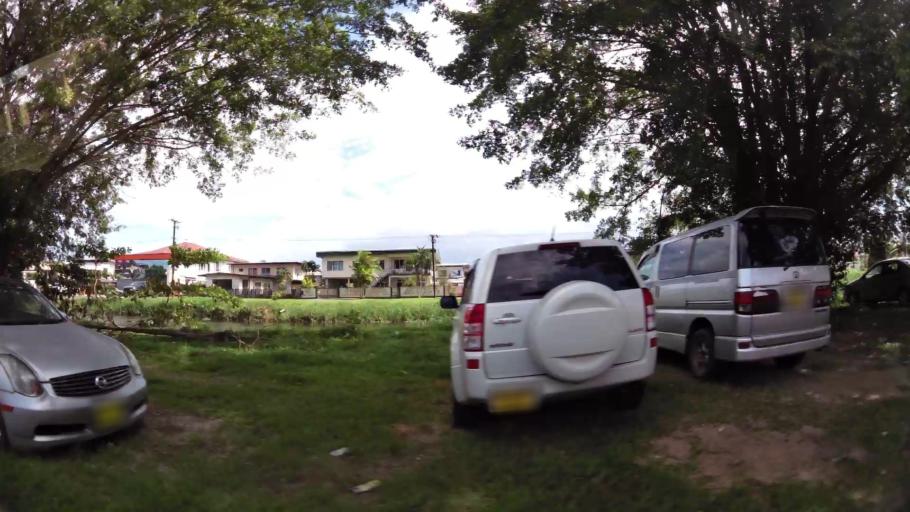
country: SR
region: Paramaribo
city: Paramaribo
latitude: 5.8438
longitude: -55.1448
